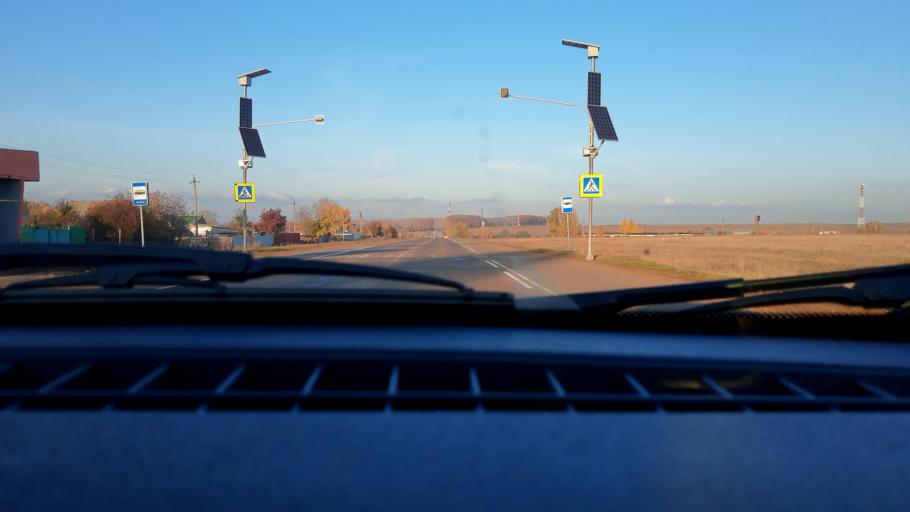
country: RU
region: Bashkortostan
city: Asanovo
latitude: 54.8078
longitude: 55.5690
